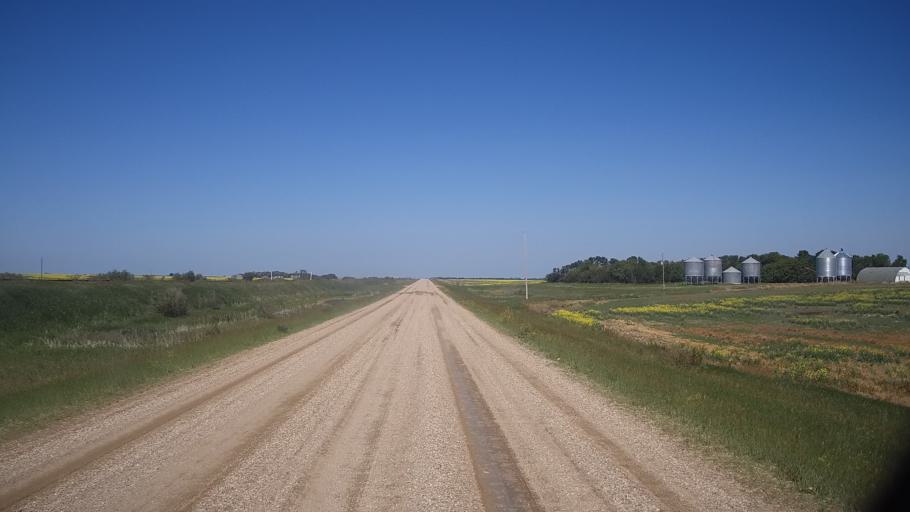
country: CA
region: Saskatchewan
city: Watrous
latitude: 51.8623
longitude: -105.9683
